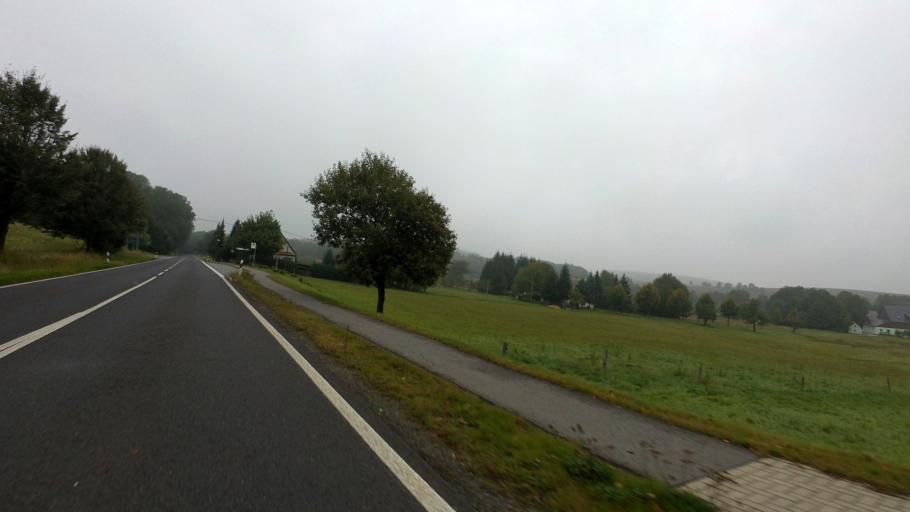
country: DE
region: Saxony
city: Sebnitz
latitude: 50.9989
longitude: 14.2448
